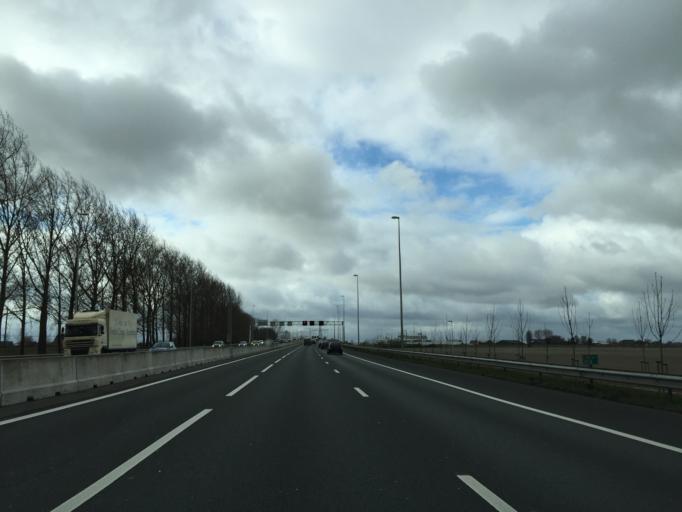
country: NL
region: South Holland
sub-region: Gemeente Lansingerland
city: Bleiswijk
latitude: 52.0245
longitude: 4.5876
